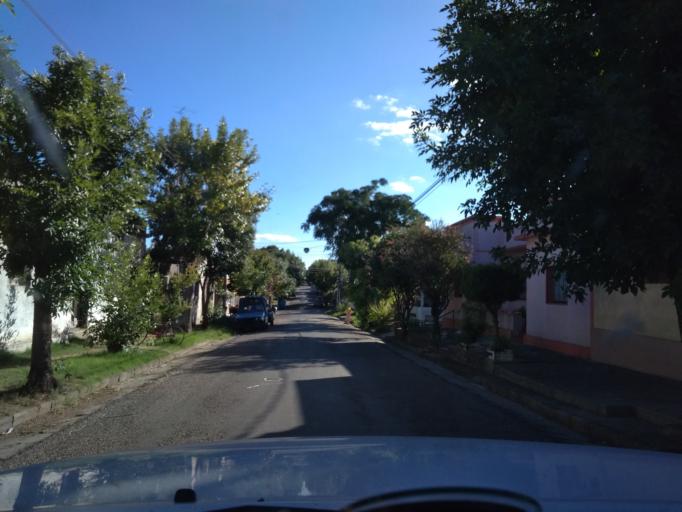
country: UY
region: Florida
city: Florida
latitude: -34.0945
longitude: -56.2097
